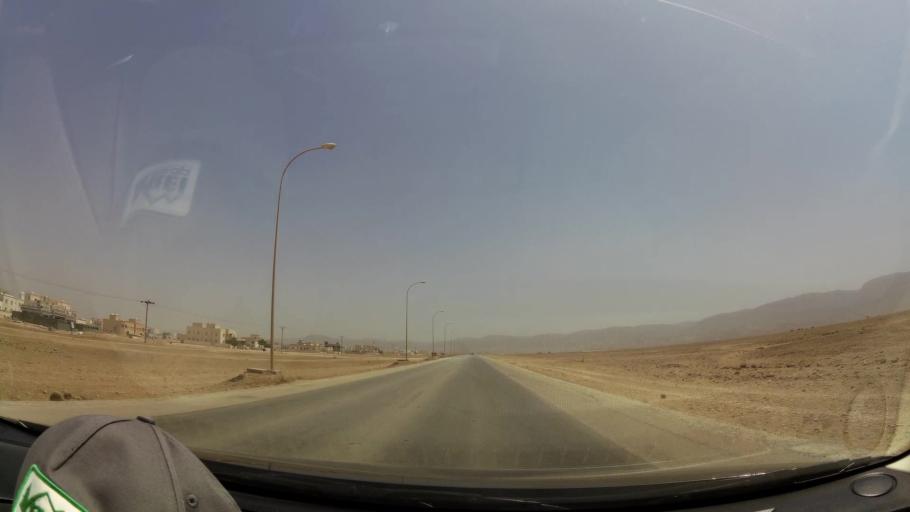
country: OM
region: Zufar
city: Salalah
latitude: 17.0724
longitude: 54.2171
